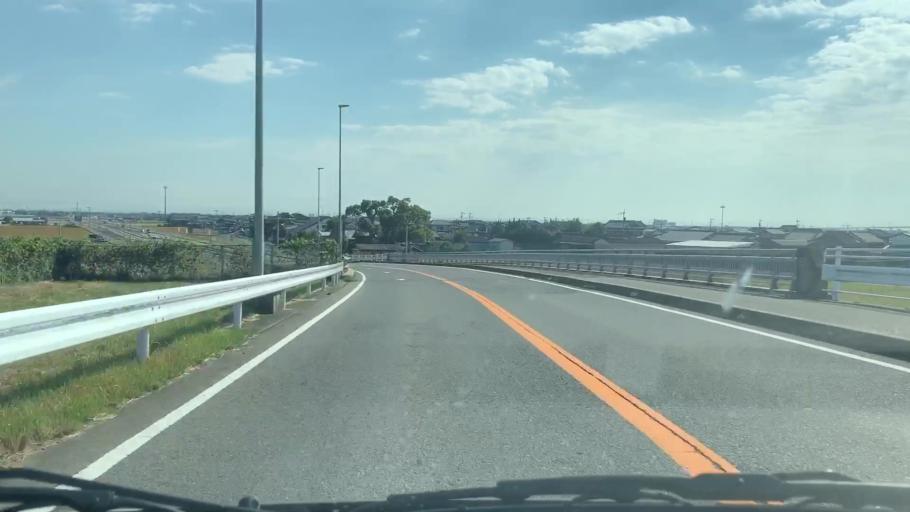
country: JP
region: Saga Prefecture
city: Saga-shi
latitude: 33.2217
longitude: 130.1946
